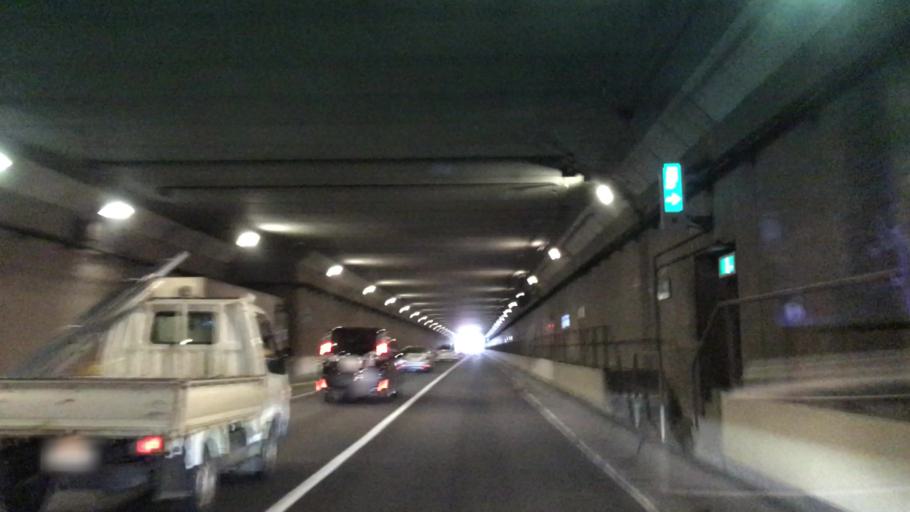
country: JP
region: Hokkaido
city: Sapporo
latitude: 43.0586
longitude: 141.3577
